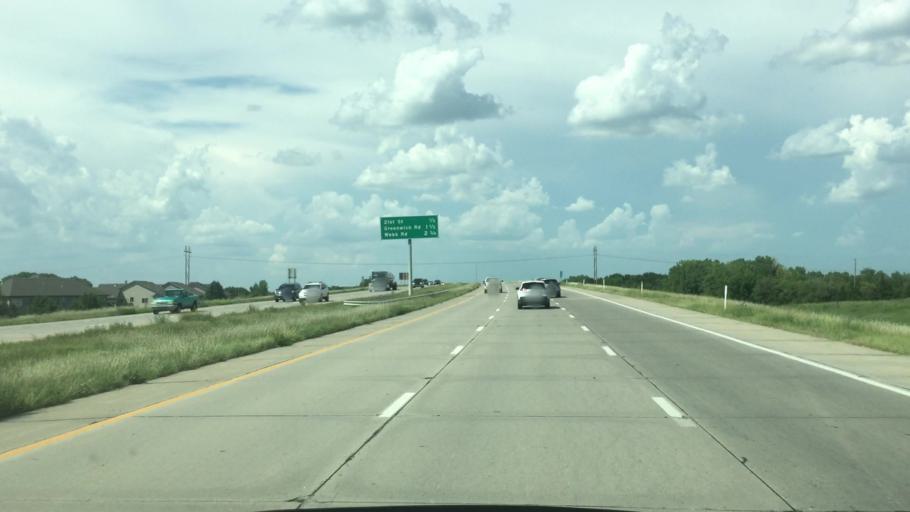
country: US
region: Kansas
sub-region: Butler County
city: Andover
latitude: 37.7123
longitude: -97.1998
